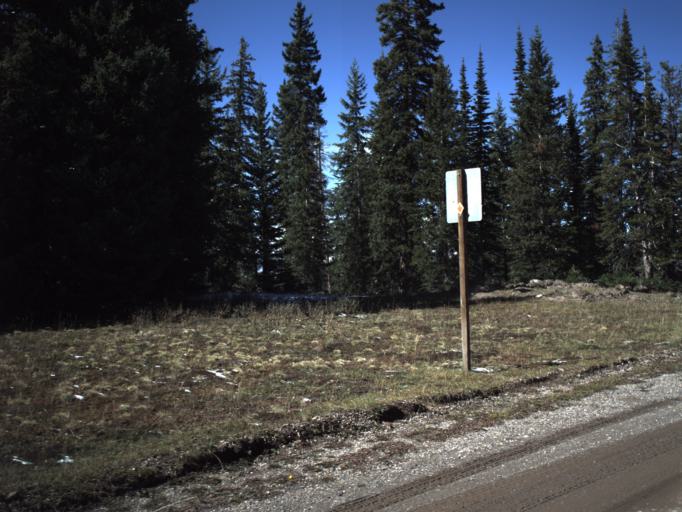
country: US
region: Utah
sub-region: Piute County
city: Junction
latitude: 38.3014
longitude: -112.3601
